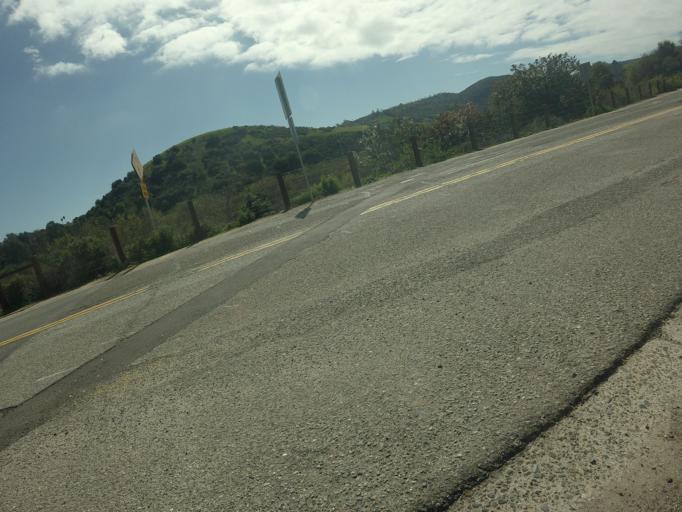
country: US
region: California
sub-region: Orange County
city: Aliso Viejo
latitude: 33.5521
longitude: -117.7189
